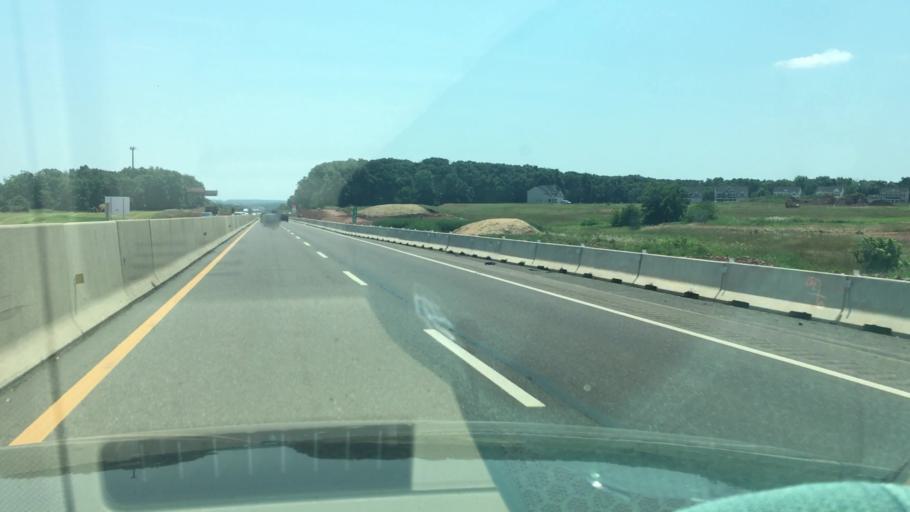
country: US
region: Pennsylvania
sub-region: Montgomery County
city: Harleysville
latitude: 40.2859
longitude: -75.3636
